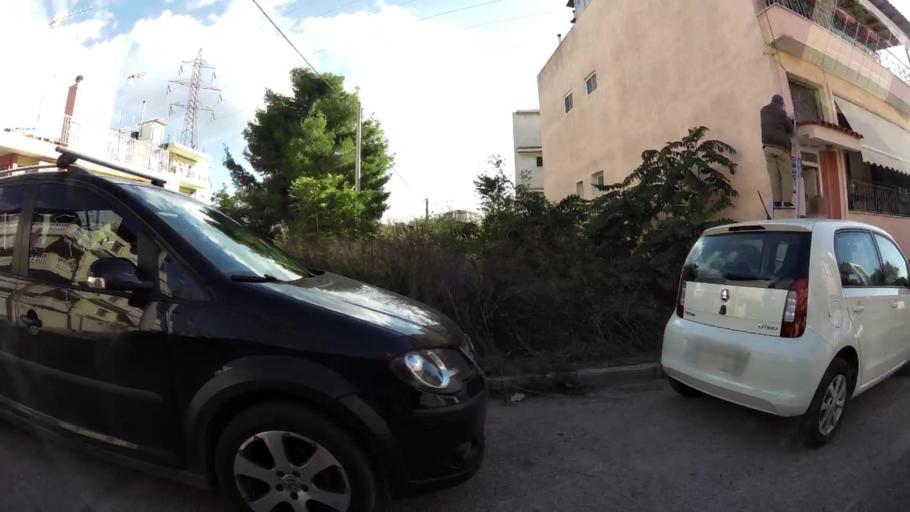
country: GR
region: Attica
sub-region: Nomarchia Anatolikis Attikis
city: Acharnes
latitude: 38.0708
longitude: 23.7458
